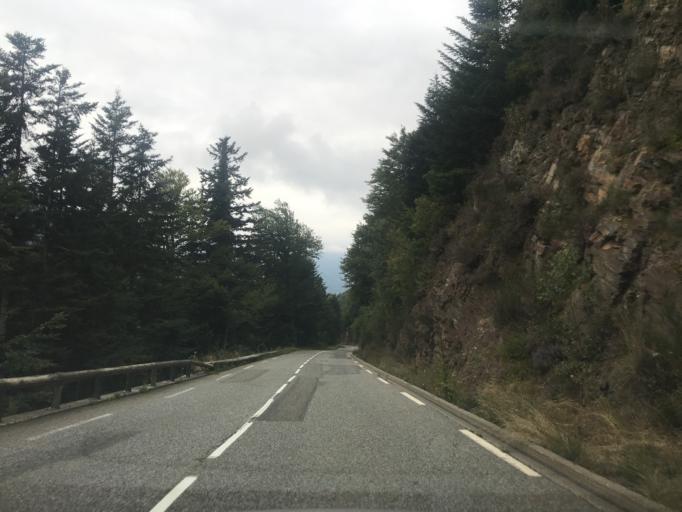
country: FR
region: Midi-Pyrenees
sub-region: Departement de la Haute-Garonne
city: Bagneres-de-Luchon
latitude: 42.7716
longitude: 0.6561
